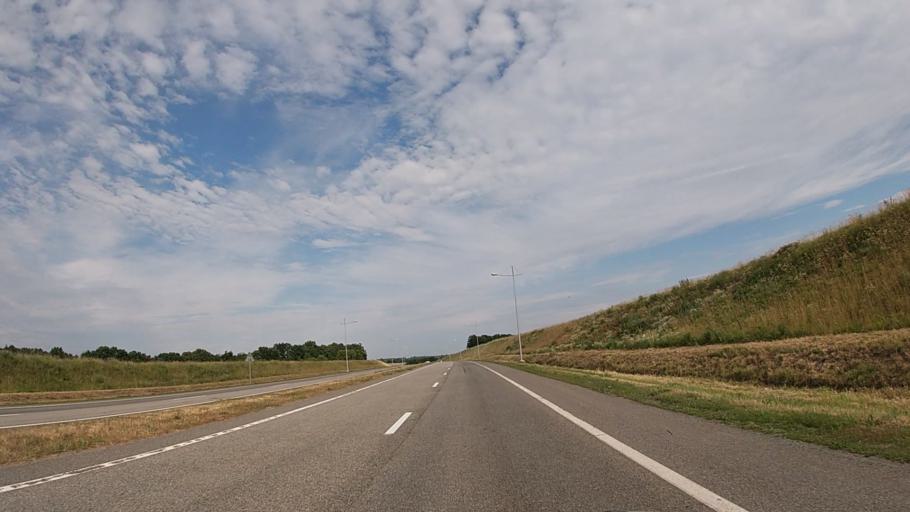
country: RU
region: Belgorod
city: Tomarovka
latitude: 50.7055
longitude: 36.2166
